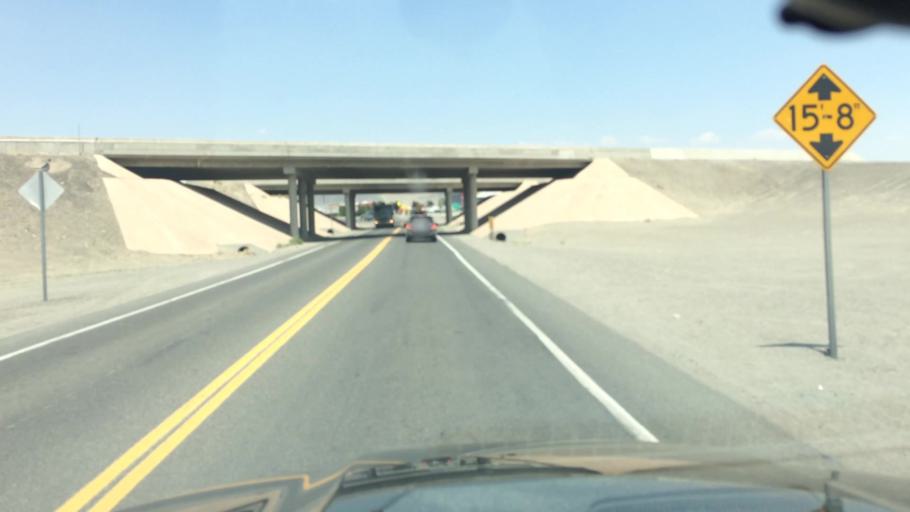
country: US
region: Nevada
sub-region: Lyon County
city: Fernley
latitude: 39.6124
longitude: -119.2184
